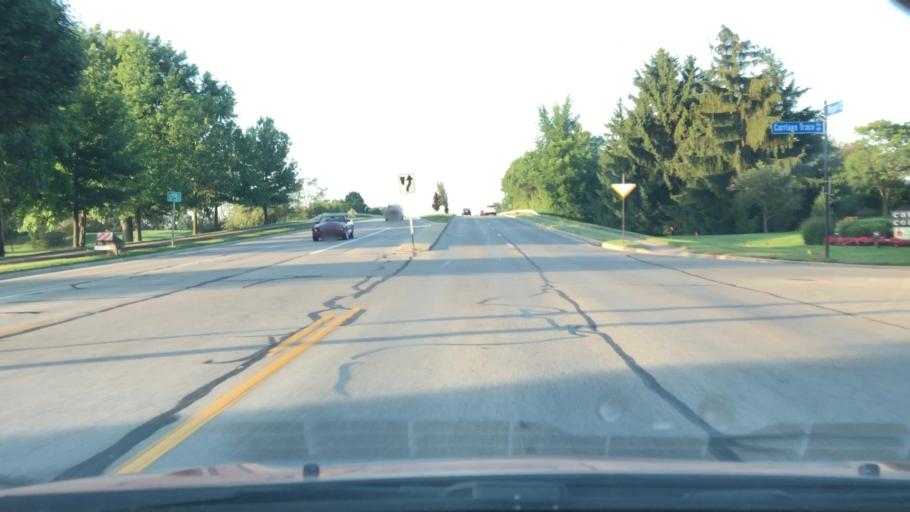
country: US
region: Ohio
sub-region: Montgomery County
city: Centerville
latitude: 39.6558
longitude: -84.1273
